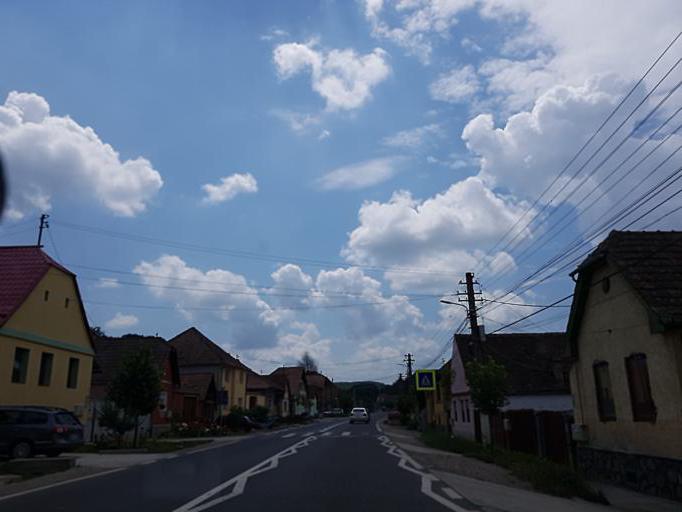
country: RO
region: Sibiu
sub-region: Comuna Slimnic
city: Slimnic
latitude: 45.9177
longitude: 24.1549
